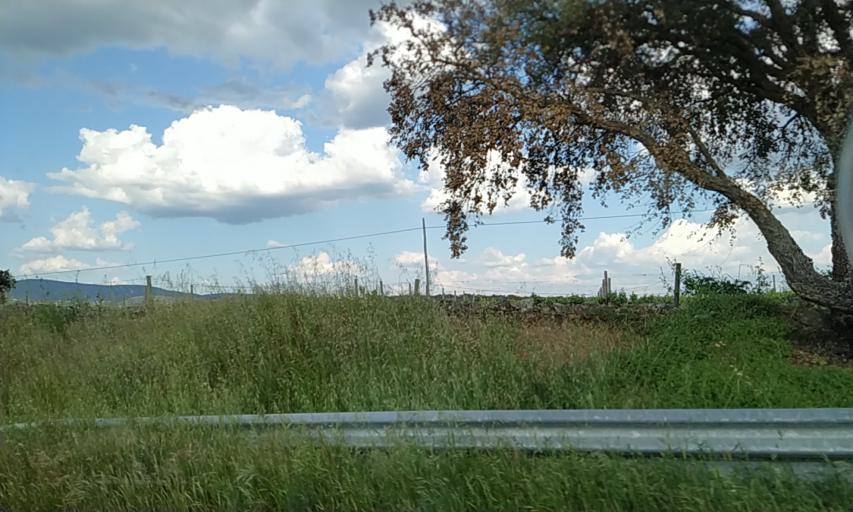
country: PT
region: Portalegre
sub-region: Portalegre
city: Portalegre
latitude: 39.2462
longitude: -7.4495
